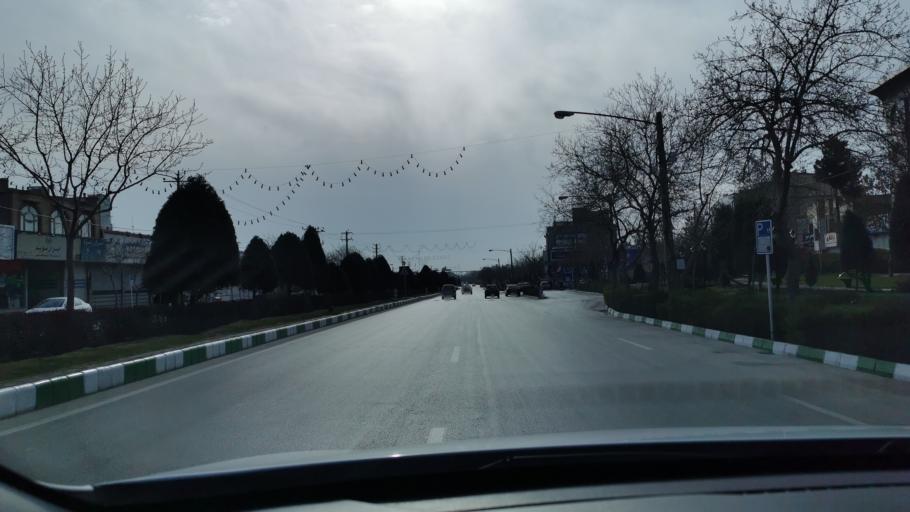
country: IR
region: Razavi Khorasan
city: Mashhad
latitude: 36.3032
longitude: 59.5155
